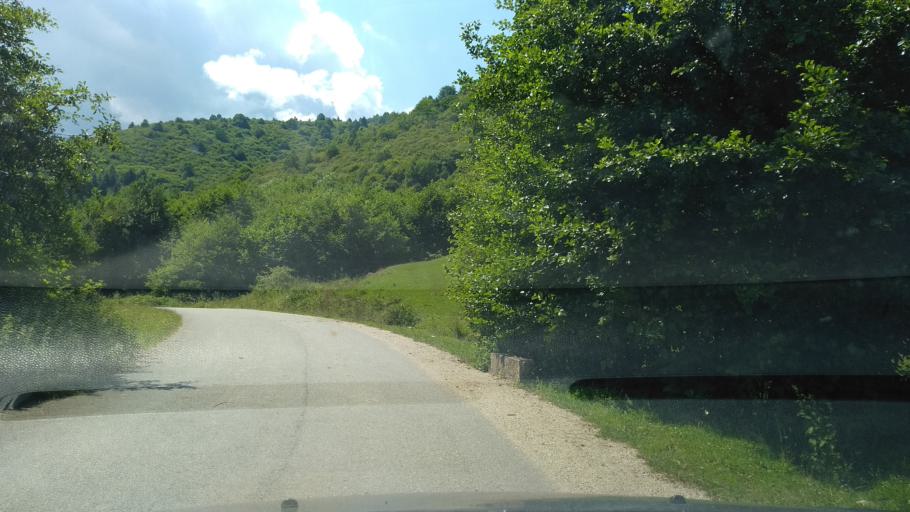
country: RO
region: Hunedoara
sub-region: Comuna Rau de Mori
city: Rau de Mori
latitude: 45.4670
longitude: 22.8958
